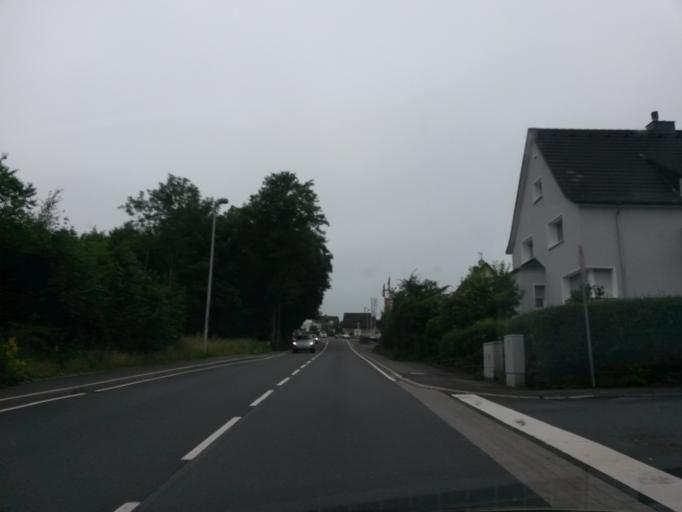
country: DE
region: North Rhine-Westphalia
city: Meinerzhagen
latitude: 51.1090
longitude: 7.6329
